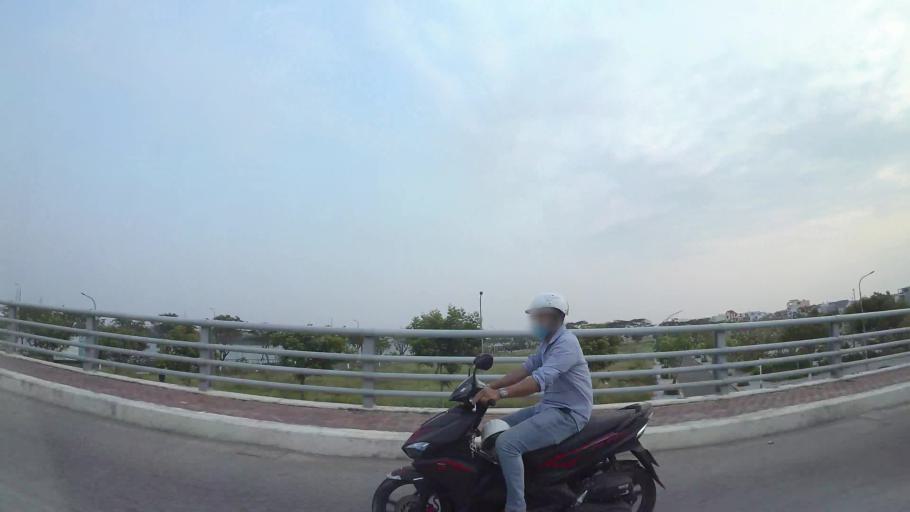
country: VN
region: Da Nang
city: Ngu Hanh Son
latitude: 16.0345
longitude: 108.2348
